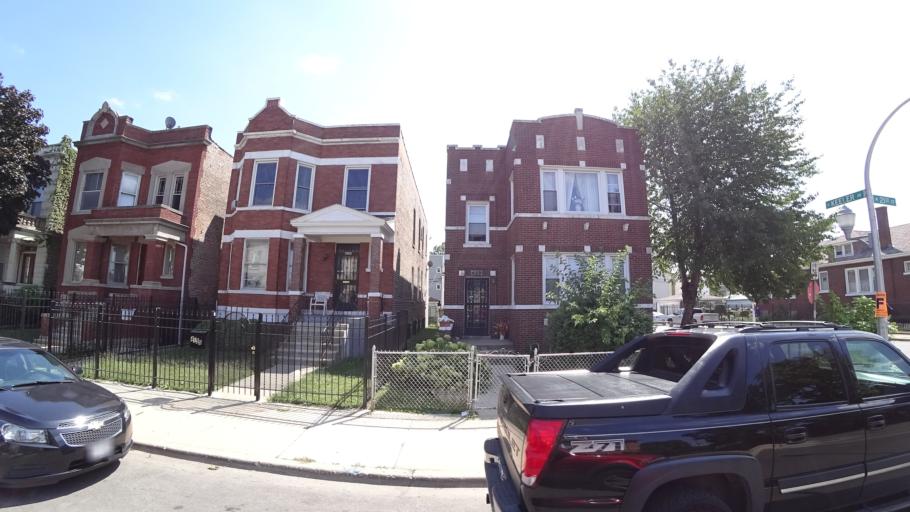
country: US
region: Illinois
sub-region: Cook County
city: Cicero
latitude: 41.8534
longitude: -87.7295
